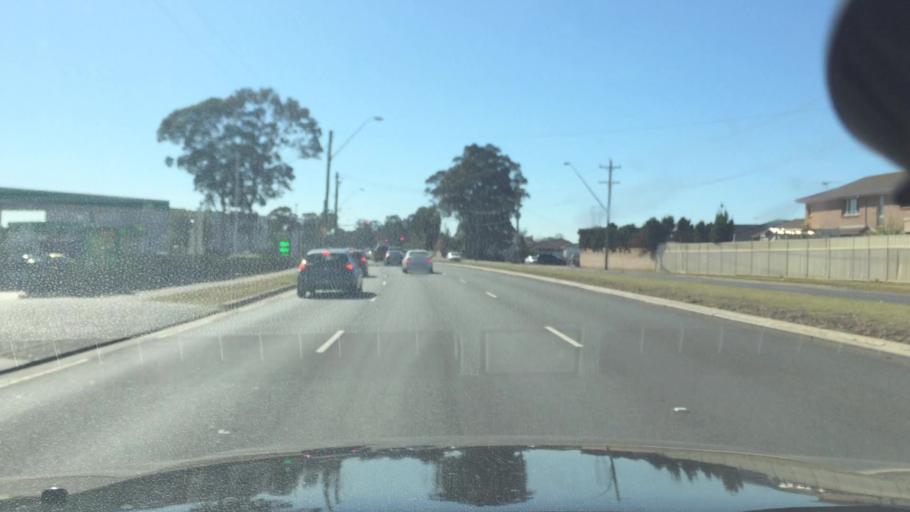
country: AU
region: New South Wales
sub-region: Campbelltown Municipality
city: Glenfield
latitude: -33.9557
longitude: 150.8944
